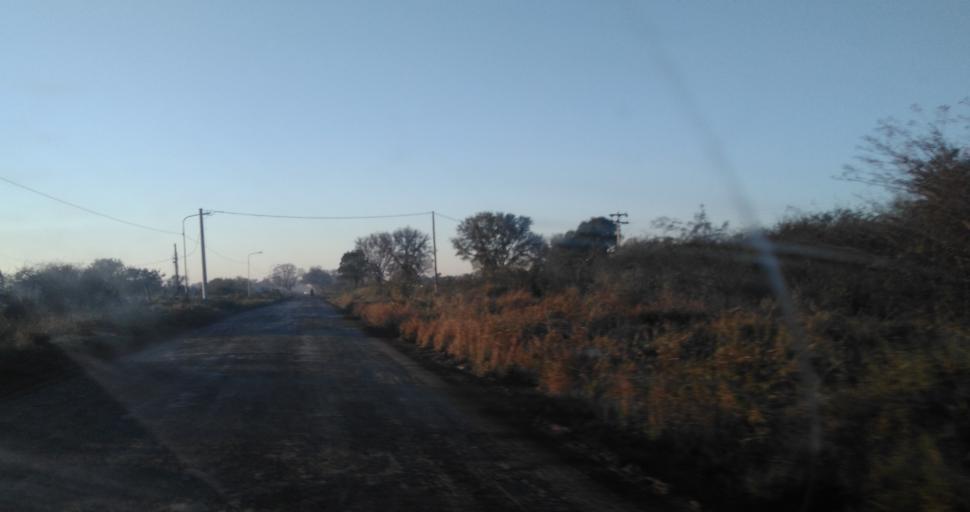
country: AR
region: Chaco
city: Fontana
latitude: -27.4337
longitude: -59.0348
